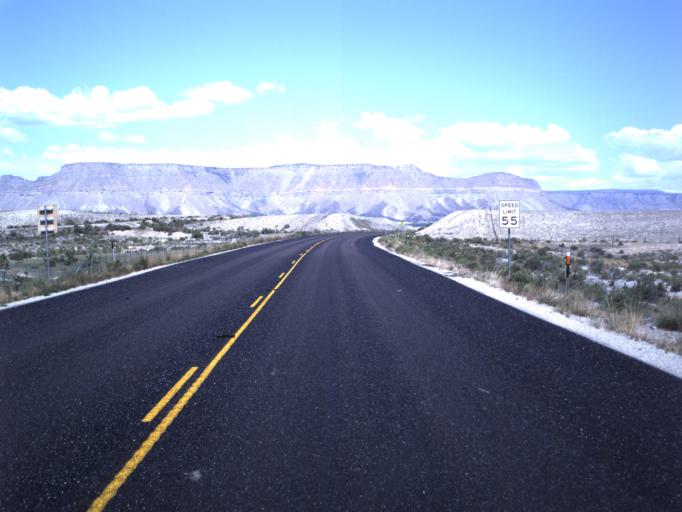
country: US
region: Utah
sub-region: Emery County
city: Ferron
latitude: 39.0601
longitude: -111.1291
